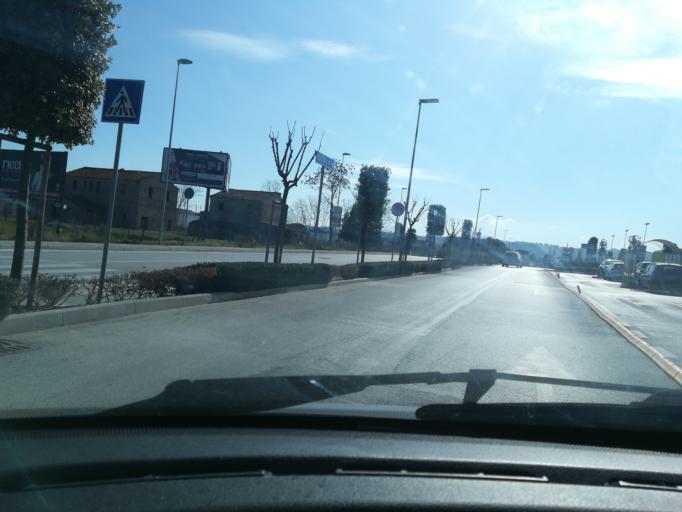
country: IT
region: The Marches
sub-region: Provincia di Macerata
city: Santa Maria Apparente
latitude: 43.2937
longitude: 13.7025
